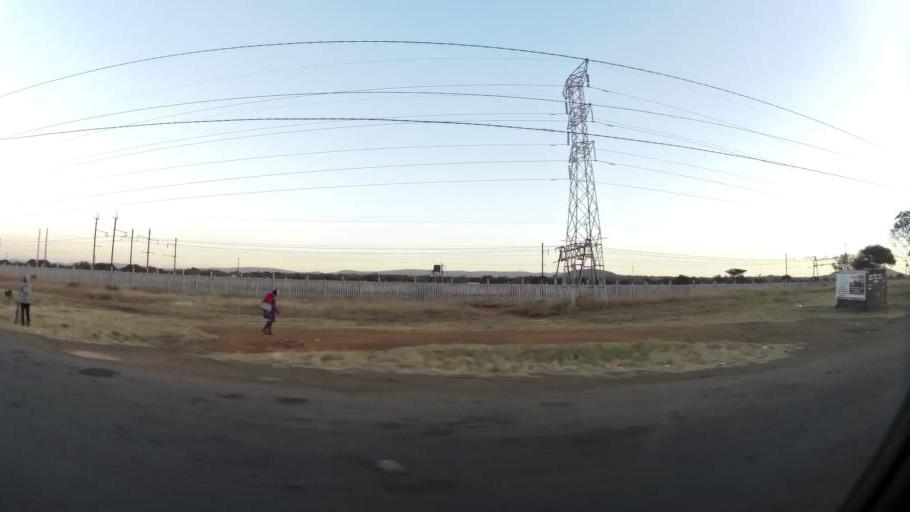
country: ZA
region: North-West
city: Ga-Rankuwa
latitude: -25.6207
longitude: 28.0111
